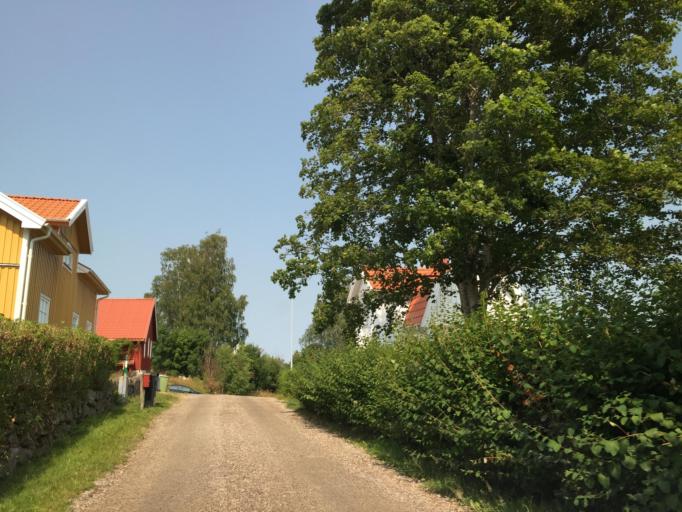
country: SE
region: Vaestra Goetaland
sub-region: Lilla Edets Kommun
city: Lilla Edet
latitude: 58.1802
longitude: 12.1121
